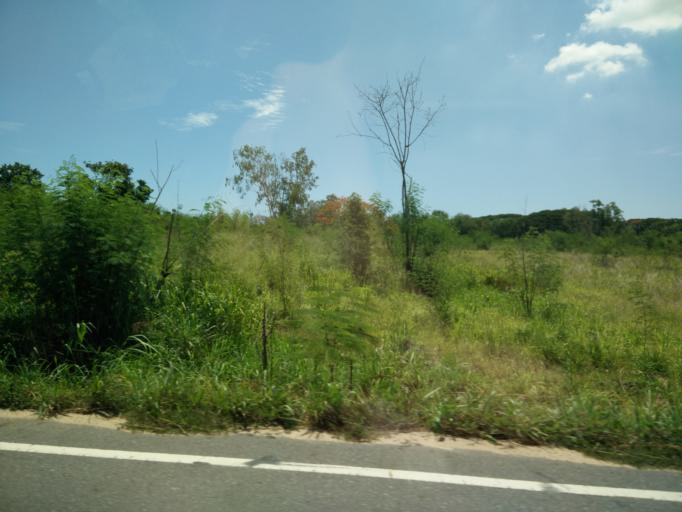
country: TH
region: Chon Buri
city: Phatthaya
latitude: 12.9052
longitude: 100.9881
